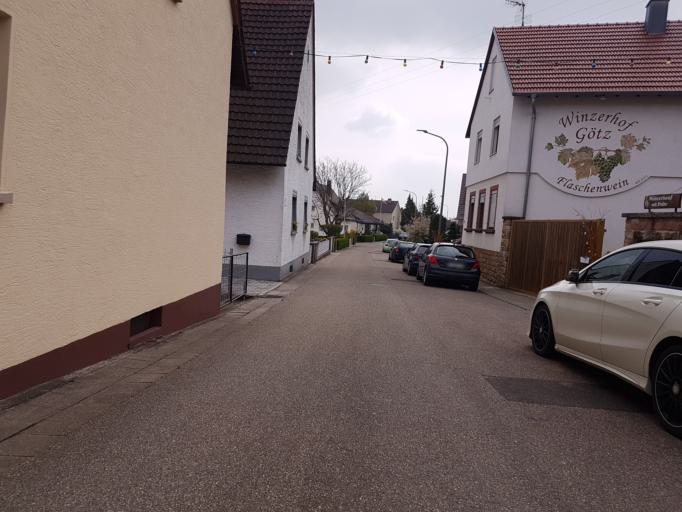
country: DE
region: Rheinland-Pfalz
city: Gleisweiler
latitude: 49.2401
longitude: 8.0640
